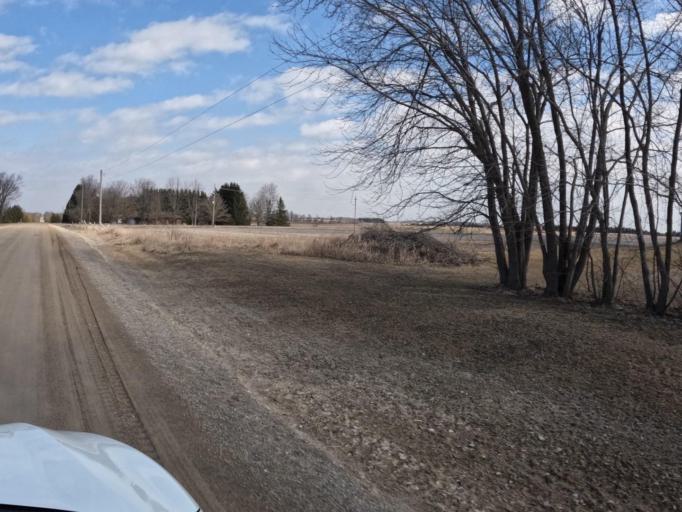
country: CA
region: Ontario
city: Orangeville
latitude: 43.9141
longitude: -80.2540
